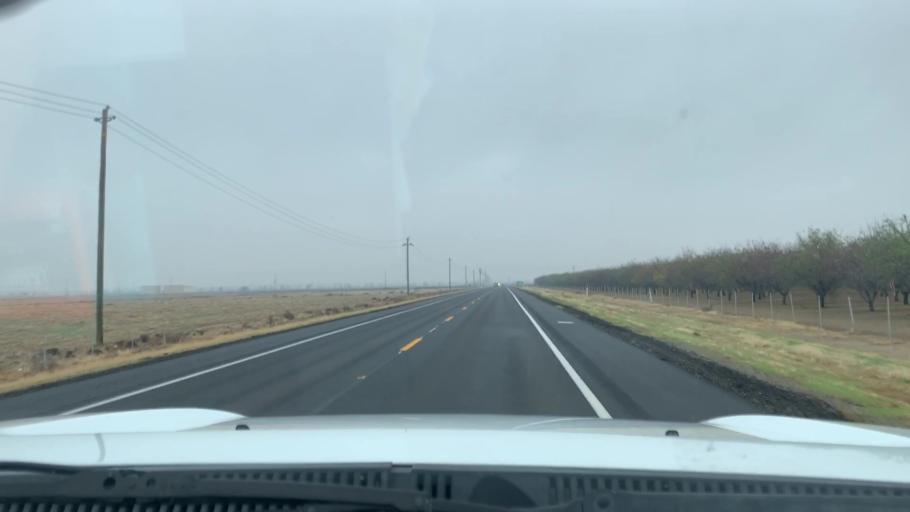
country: US
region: California
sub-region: Kern County
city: Lost Hills
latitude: 35.6157
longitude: -119.7506
